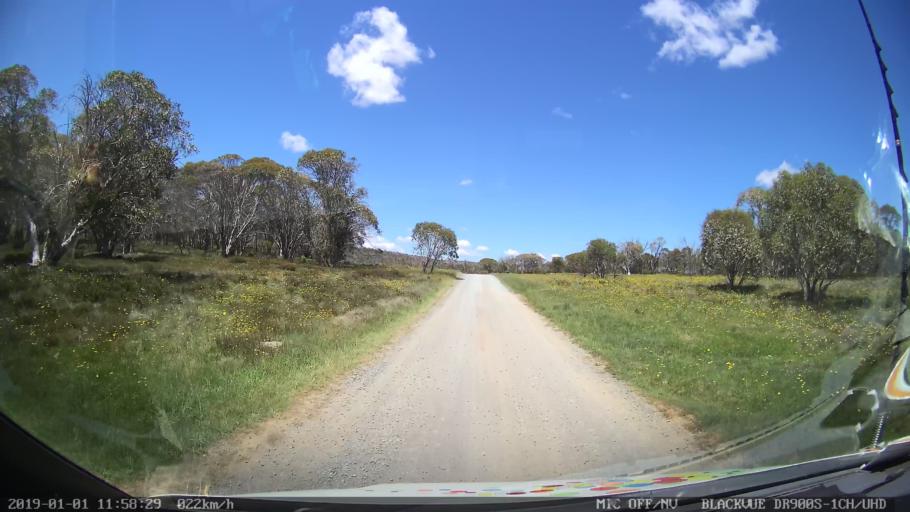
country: AU
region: New South Wales
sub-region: Snowy River
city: Jindabyne
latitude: -35.8900
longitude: 148.4482
